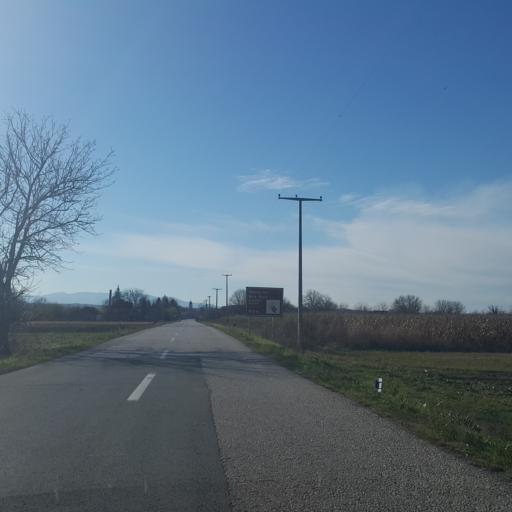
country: RS
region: Central Serbia
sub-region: Sumadijski Okrug
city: Topola
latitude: 44.2572
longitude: 20.8169
